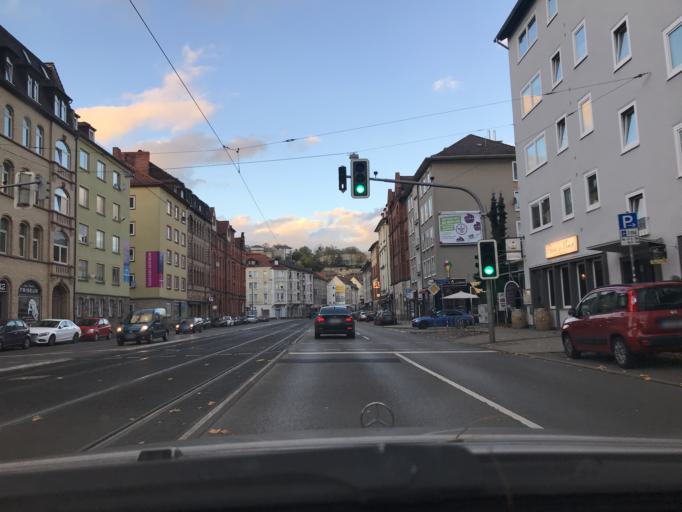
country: DE
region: Hesse
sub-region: Regierungsbezirk Kassel
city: Kassel
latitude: 51.3053
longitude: 9.4854
